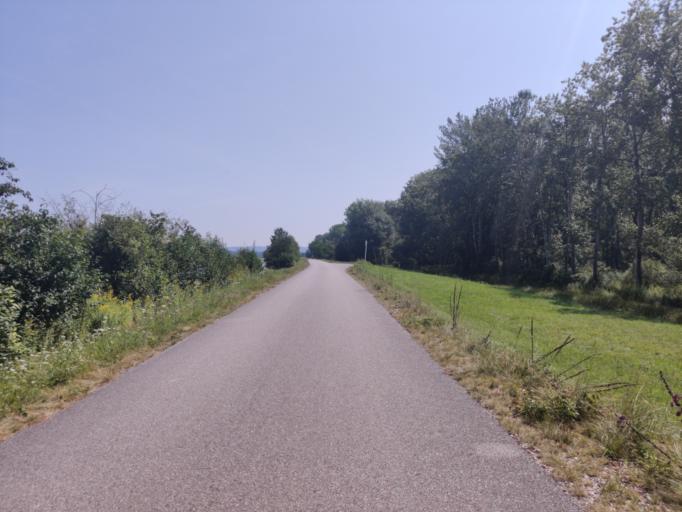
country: AT
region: Upper Austria
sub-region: Politischer Bezirk Urfahr-Umgebung
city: Goldworth
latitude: 48.3167
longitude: 14.0705
